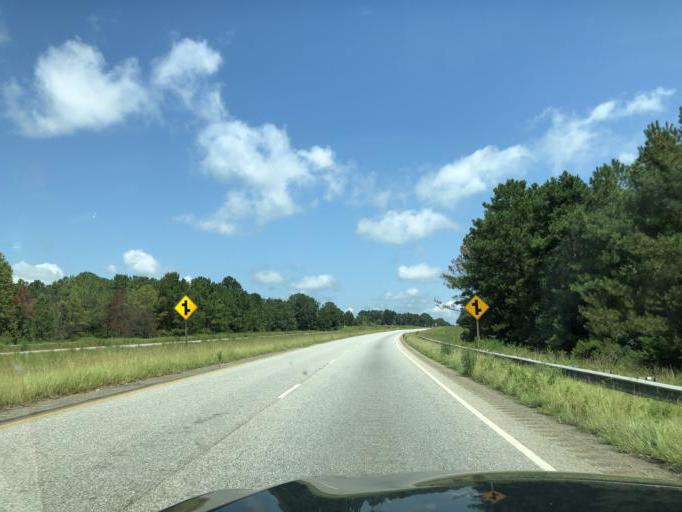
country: US
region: Alabama
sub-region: Henry County
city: Abbeville
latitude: 31.6961
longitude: -85.2785
